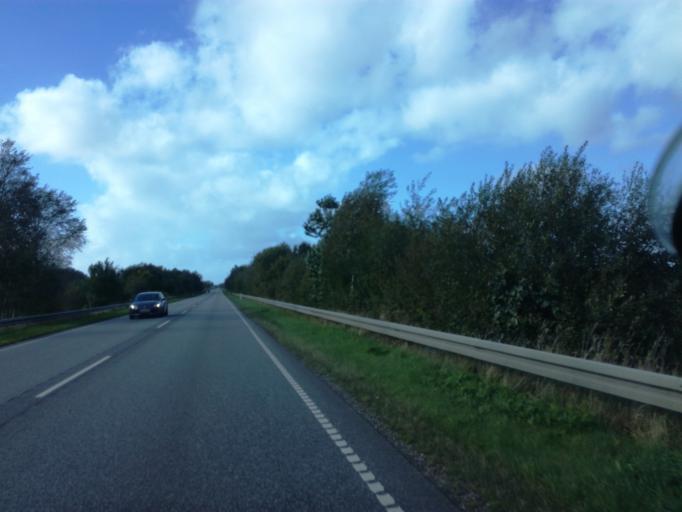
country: DK
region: South Denmark
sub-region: Vejle Kommune
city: Brejning
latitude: 55.6262
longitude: 9.7245
